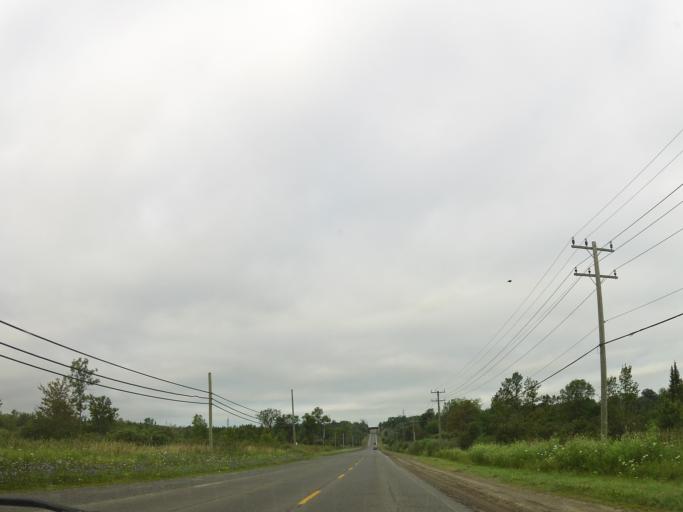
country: CA
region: Ontario
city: Kingston
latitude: 44.4059
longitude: -76.6263
